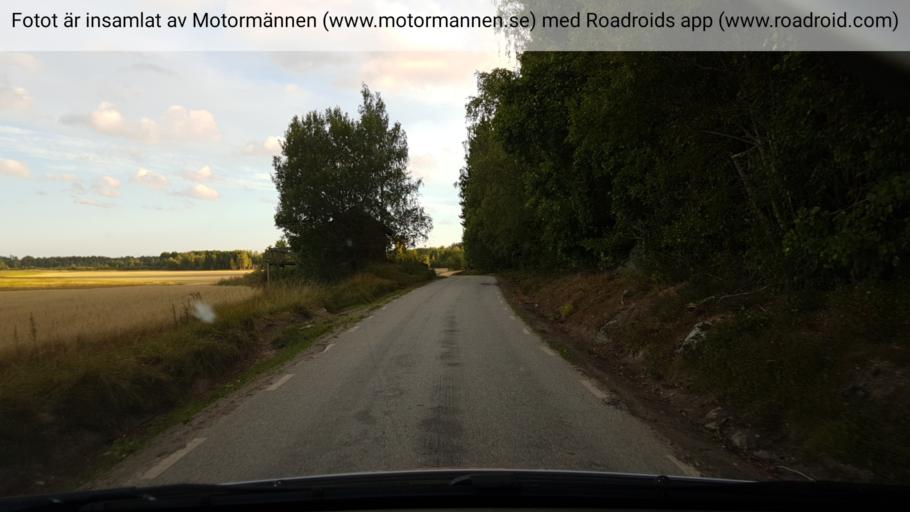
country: SE
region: Vaestmanland
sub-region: Surahammars Kommun
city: Ramnas
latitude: 59.7468
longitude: 16.1743
